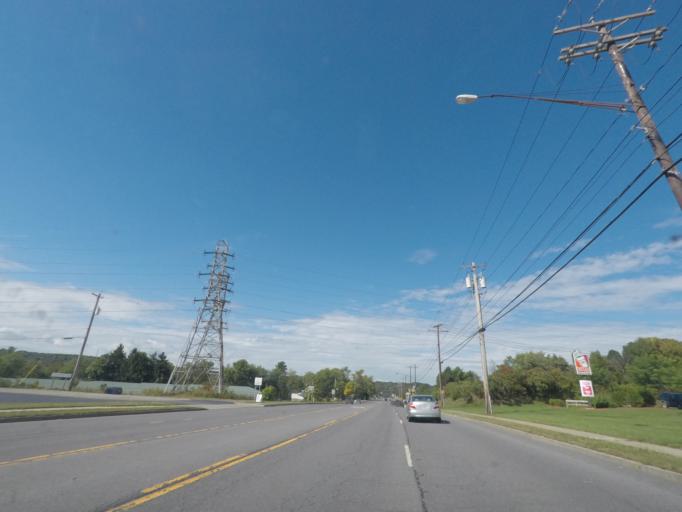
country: US
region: New York
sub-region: Rensselaer County
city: East Greenbush
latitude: 42.6036
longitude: -73.7153
